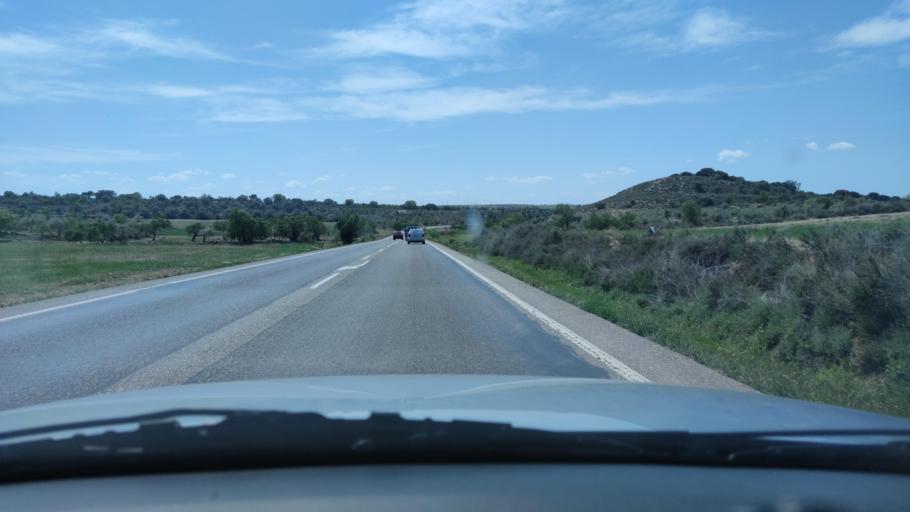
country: ES
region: Catalonia
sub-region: Provincia de Lleida
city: Tarrega
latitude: 41.6734
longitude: 1.1500
